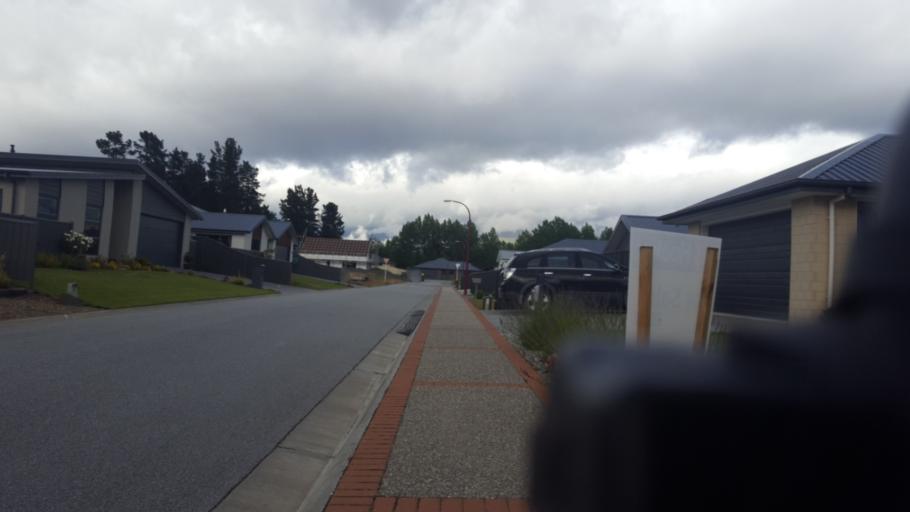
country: NZ
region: Otago
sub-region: Queenstown-Lakes District
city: Wanaka
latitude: -45.2413
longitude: 169.3799
